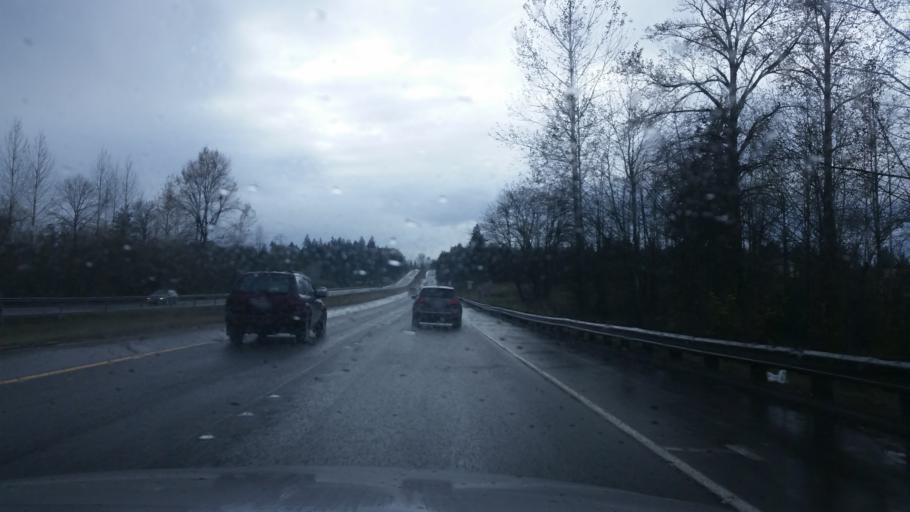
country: US
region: Washington
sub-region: King County
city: Covington
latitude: 47.3527
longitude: -122.1304
